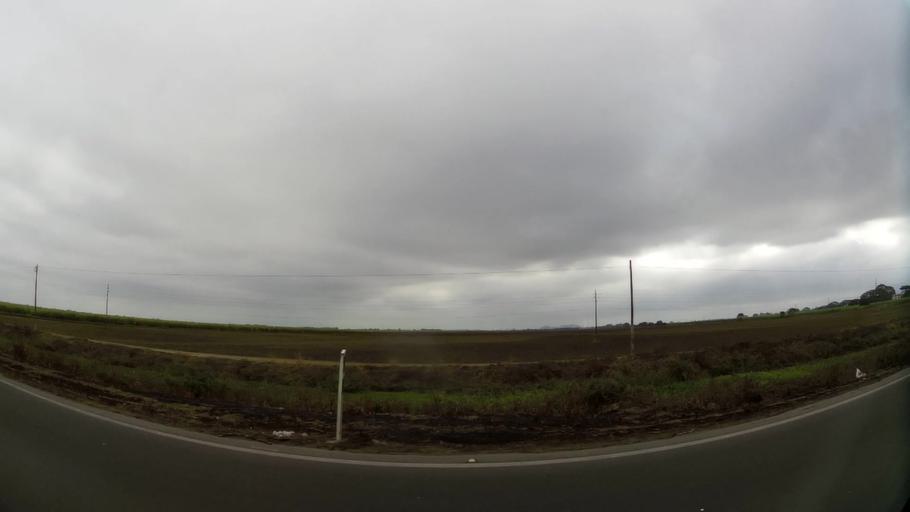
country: EC
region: Guayas
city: Coronel Marcelino Mariduena
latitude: -2.3420
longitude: -79.6348
